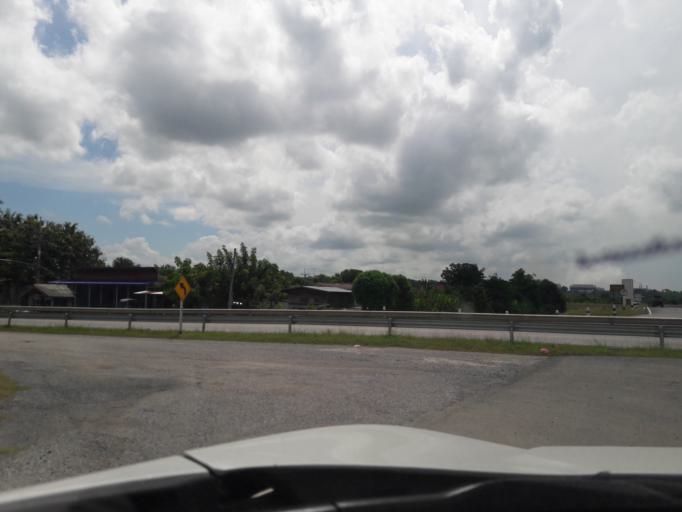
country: TH
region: Lop Buri
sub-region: Amphoe Tha Luang
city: Tha Luang
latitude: 15.0681
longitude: 101.0905
